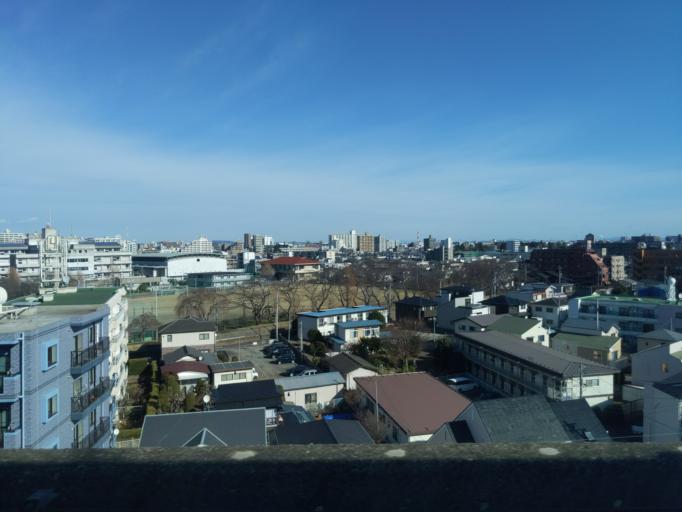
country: JP
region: Miyagi
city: Sendai
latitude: 38.2482
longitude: 140.8912
